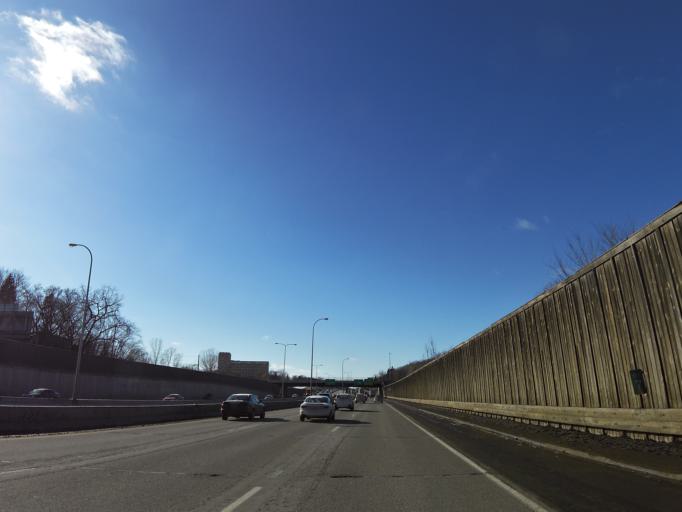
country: US
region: Minnesota
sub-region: Hennepin County
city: Saint Louis Park
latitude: 44.9704
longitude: -93.3184
